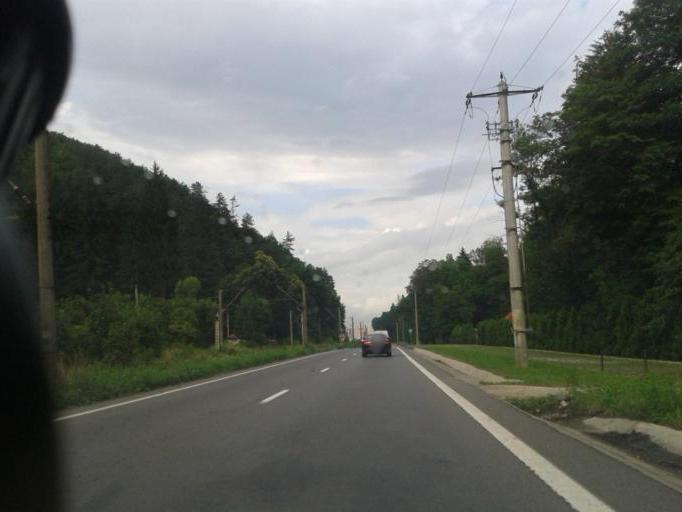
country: RO
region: Brasov
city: Brasov
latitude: 45.5981
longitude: 25.6417
